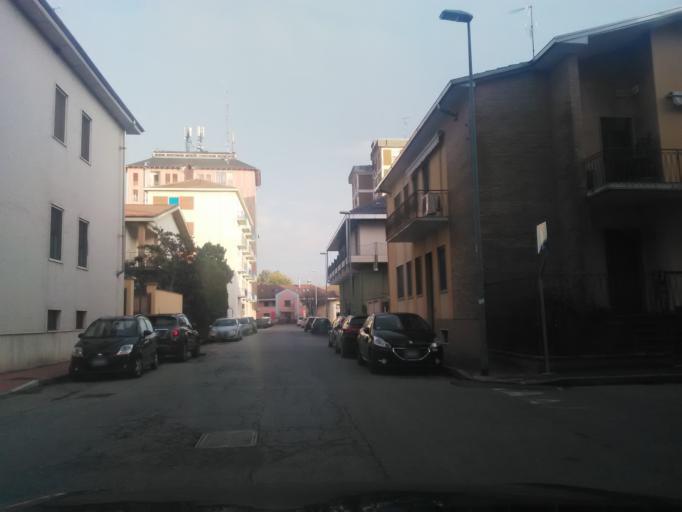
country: IT
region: Piedmont
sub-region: Provincia di Vercelli
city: Vercelli
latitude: 45.3157
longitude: 8.4252
